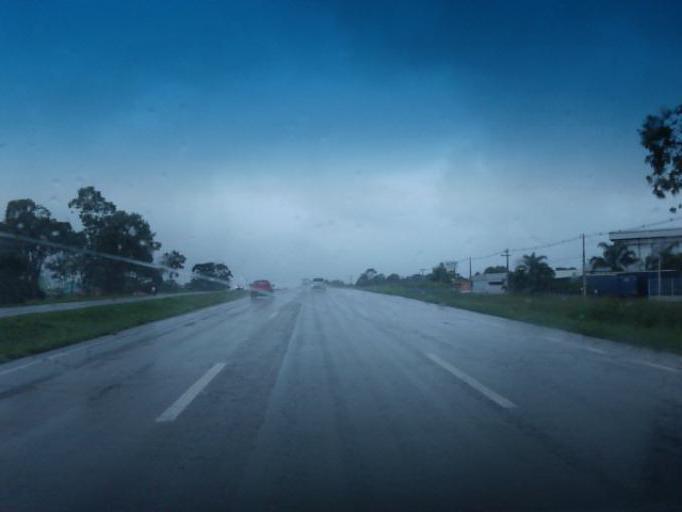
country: BR
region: Parana
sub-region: Sao Jose Dos Pinhais
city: Sao Jose dos Pinhais
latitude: -25.5655
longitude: -49.1626
